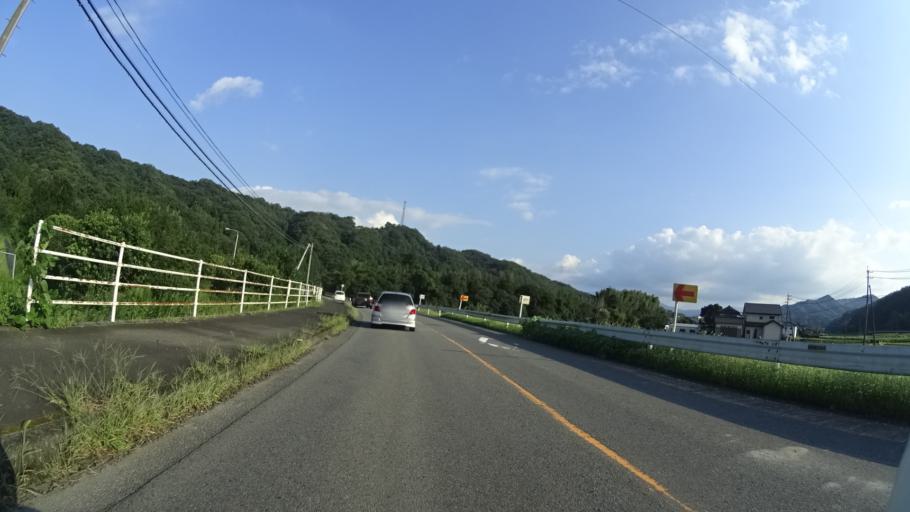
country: JP
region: Oita
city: Bungo-Takada-shi
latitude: 33.4662
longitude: 131.3287
